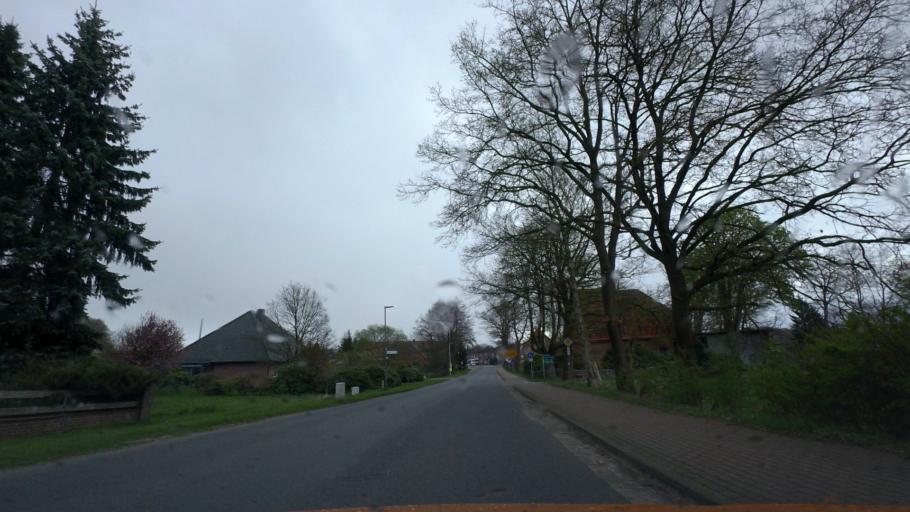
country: DE
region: Lower Saxony
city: Bispingen
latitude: 53.1121
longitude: 9.9567
